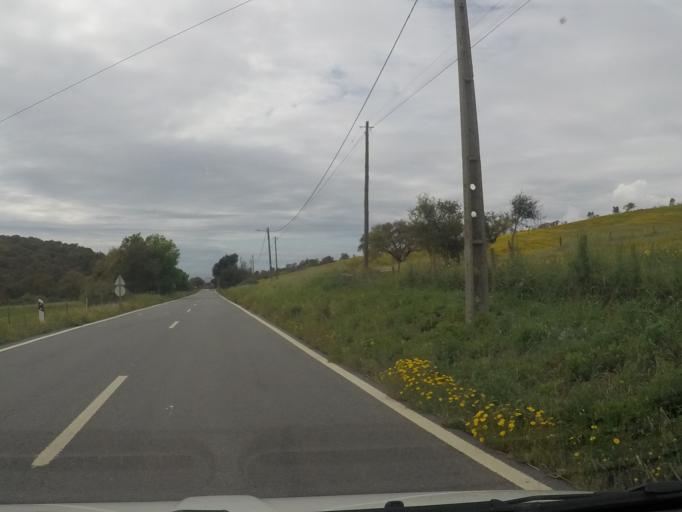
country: PT
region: Setubal
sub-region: Sines
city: Porto Covo
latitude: 37.8664
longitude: -8.7314
